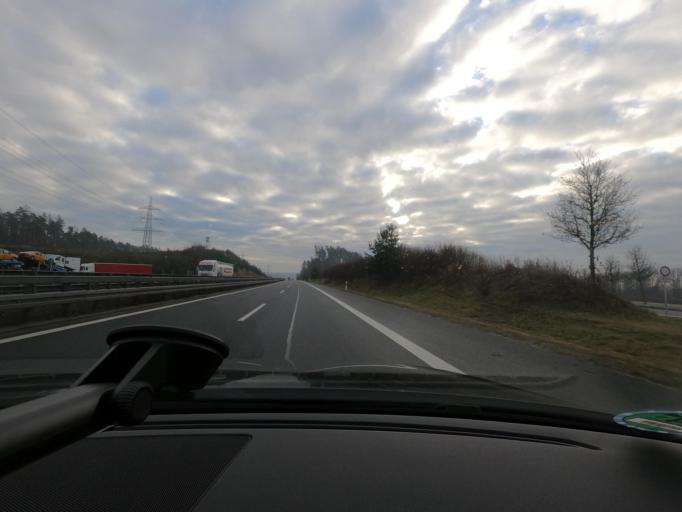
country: DE
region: Bavaria
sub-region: Upper Franconia
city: Rodental
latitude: 50.2514
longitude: 11.0302
